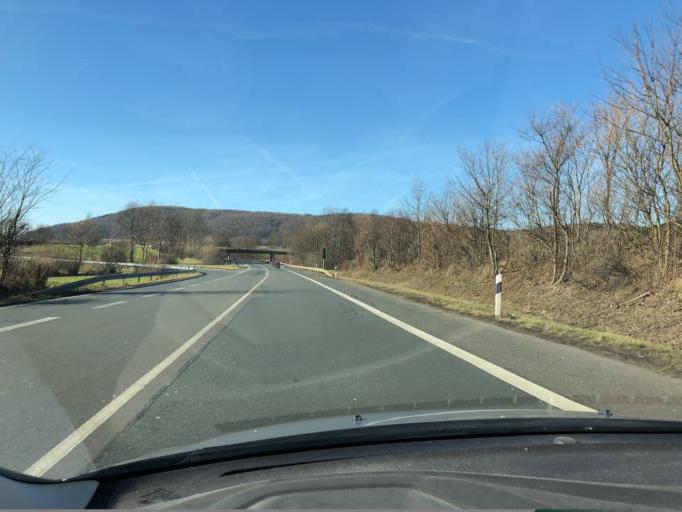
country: DE
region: Lower Saxony
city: Hahausen
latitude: 51.9562
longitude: 10.2380
